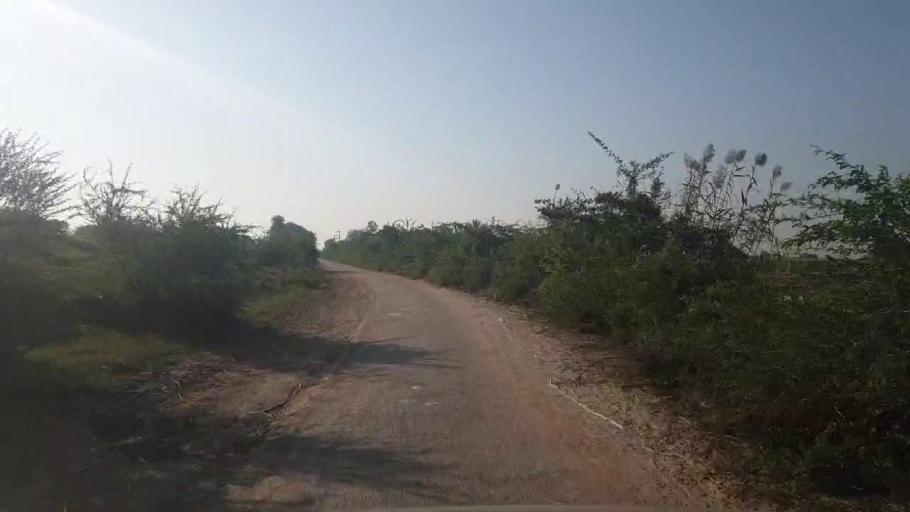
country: PK
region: Sindh
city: Tando Bago
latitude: 24.7384
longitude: 68.9304
